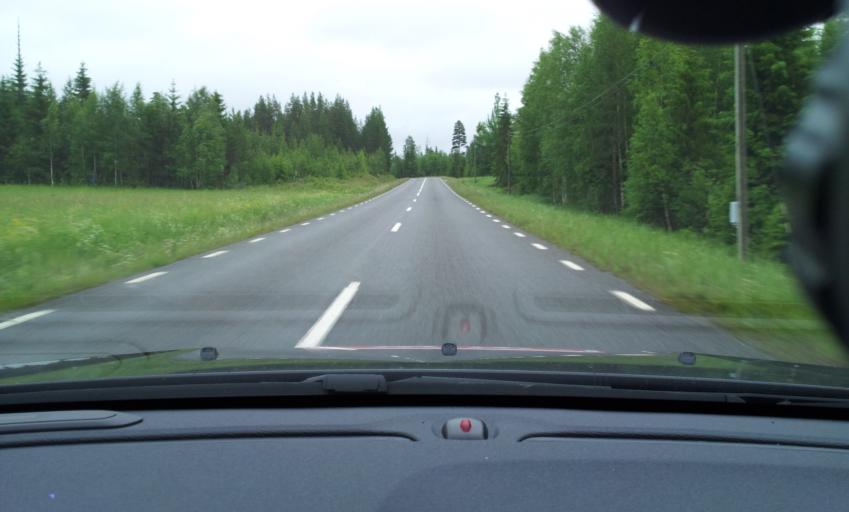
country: SE
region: Jaemtland
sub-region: Stroemsunds Kommun
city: Stroemsund
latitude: 63.3975
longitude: 15.6380
